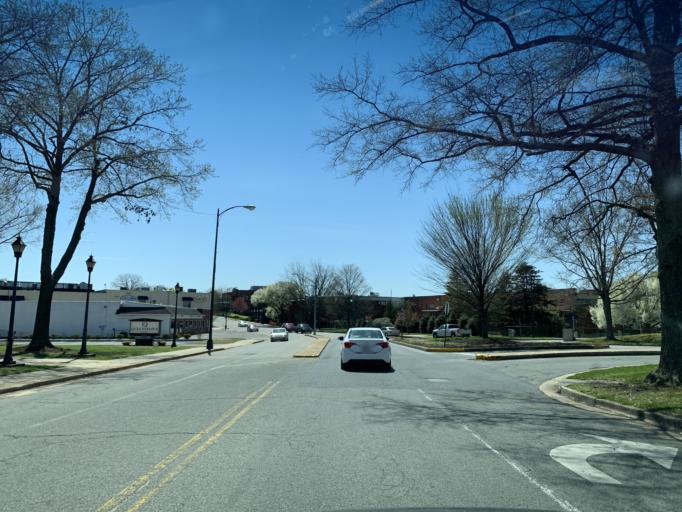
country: US
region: Maryland
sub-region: Talbot County
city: Easton
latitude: 38.7797
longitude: -76.0754
